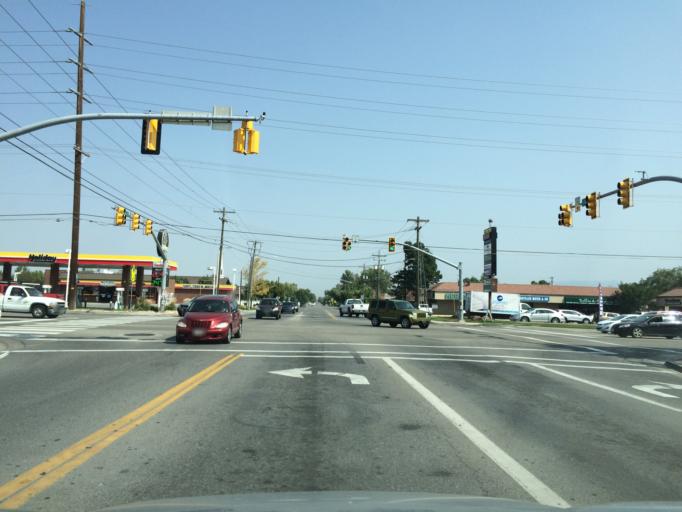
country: US
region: Utah
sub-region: Salt Lake County
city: West Jordan
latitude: 40.5875
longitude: -111.9292
